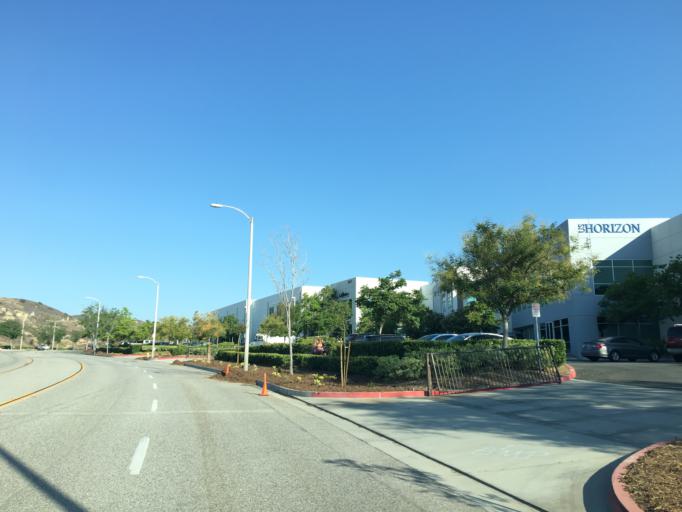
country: US
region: California
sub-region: Los Angeles County
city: Val Verde
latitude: 34.4529
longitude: -118.6334
